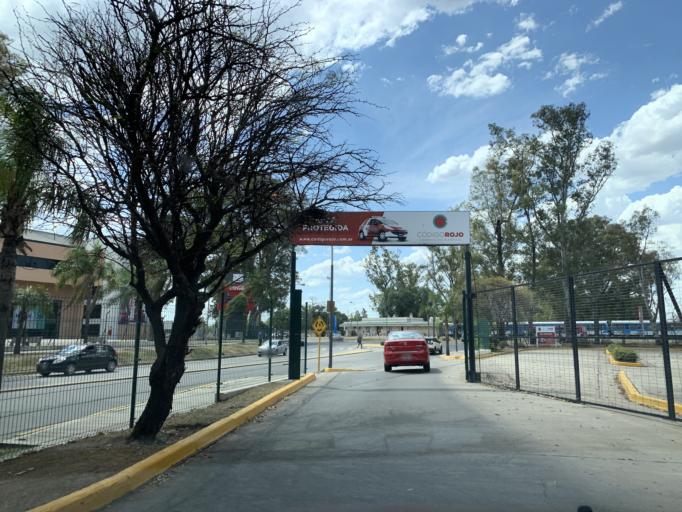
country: AR
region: Cordoba
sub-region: Departamento de Capital
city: Cordoba
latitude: -31.3656
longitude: -64.2203
